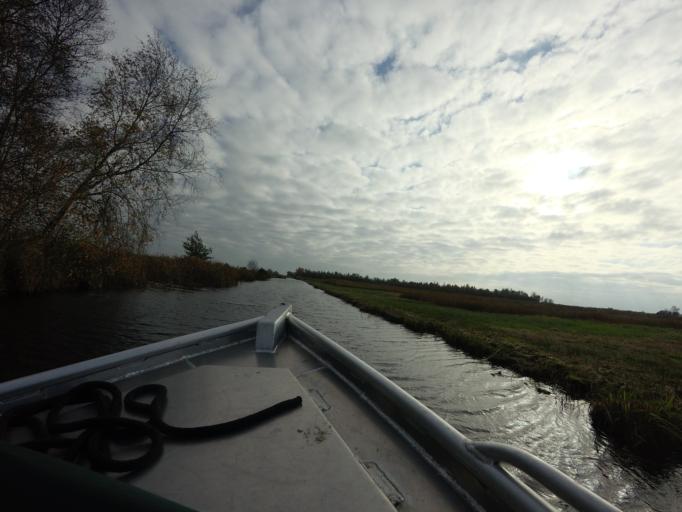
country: NL
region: Overijssel
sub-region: Gemeente Steenwijkerland
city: Oldemarkt
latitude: 52.7875
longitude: 5.8974
